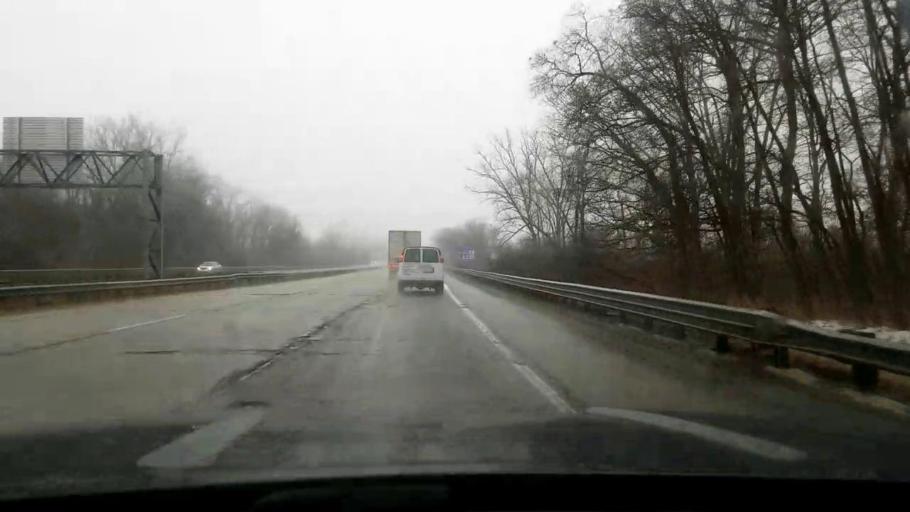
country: US
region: Michigan
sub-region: Jackson County
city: Jackson
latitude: 42.2746
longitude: -84.3587
